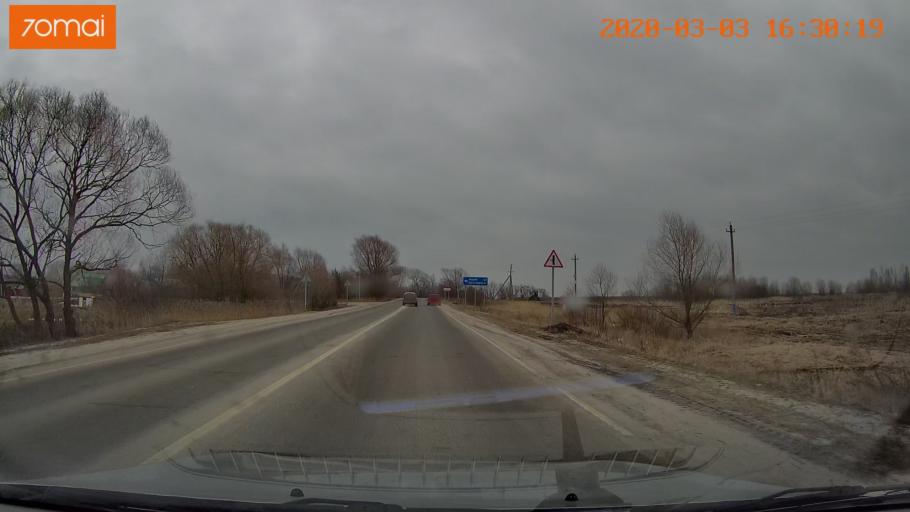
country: RU
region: Moskovskaya
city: Konobeyevo
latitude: 55.4336
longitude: 38.7102
